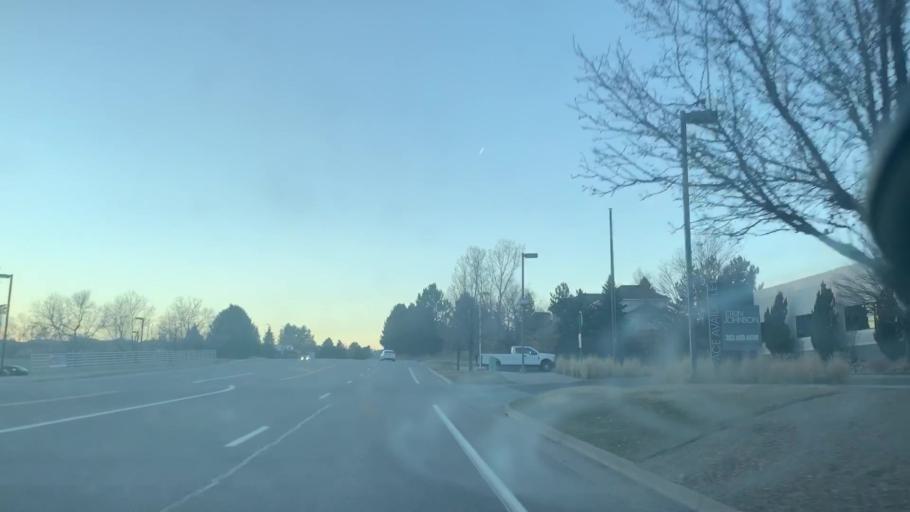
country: US
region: Colorado
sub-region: Arapahoe County
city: Centennial
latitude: 39.5984
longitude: -104.8611
